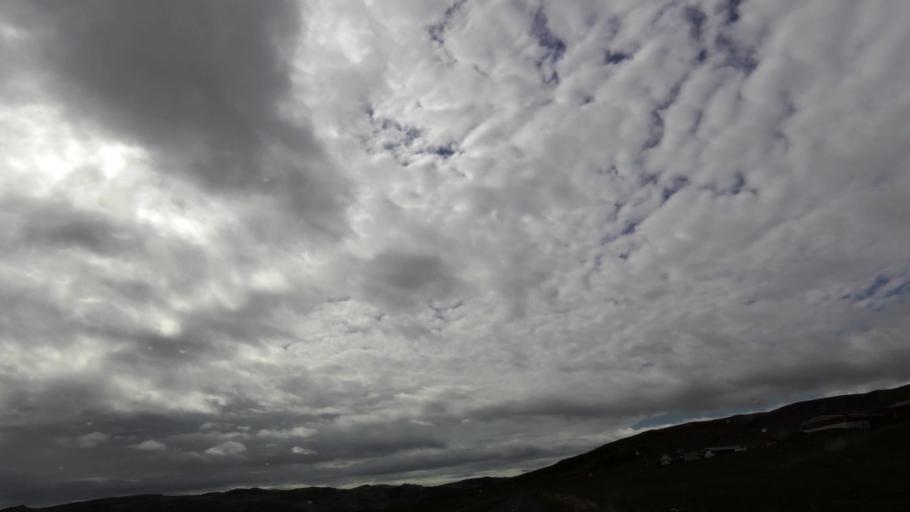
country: IS
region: West
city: Stykkisholmur
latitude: 65.5380
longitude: -22.0588
